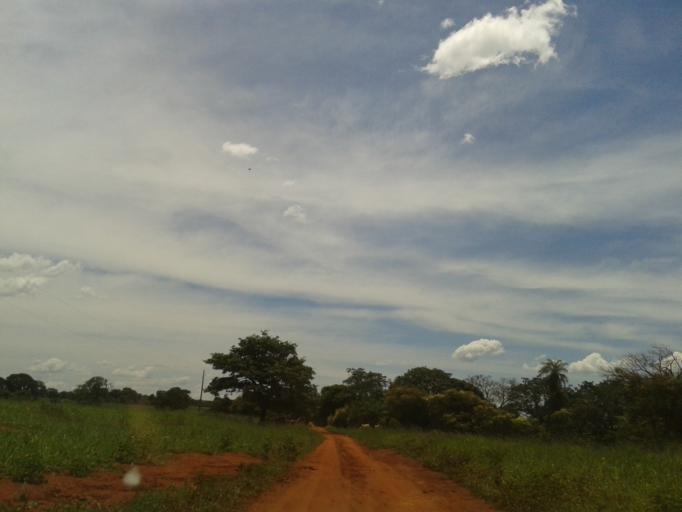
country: BR
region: Minas Gerais
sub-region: Capinopolis
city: Capinopolis
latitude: -18.8009
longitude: -49.7784
